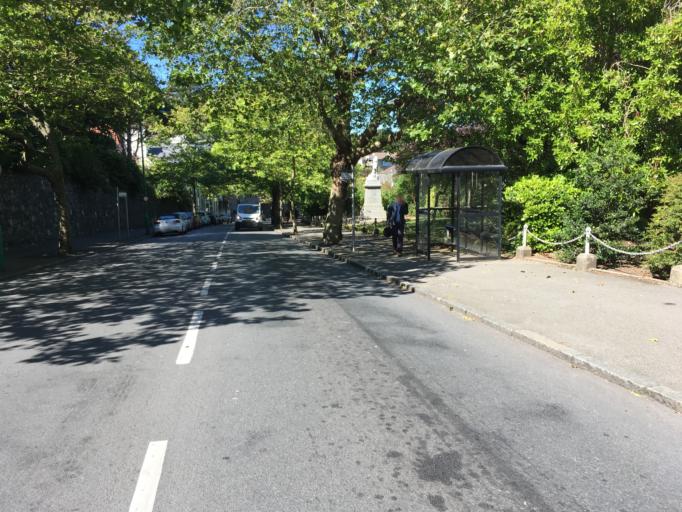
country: GG
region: St Peter Port
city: Saint Peter Port
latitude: 49.4576
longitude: -2.5391
